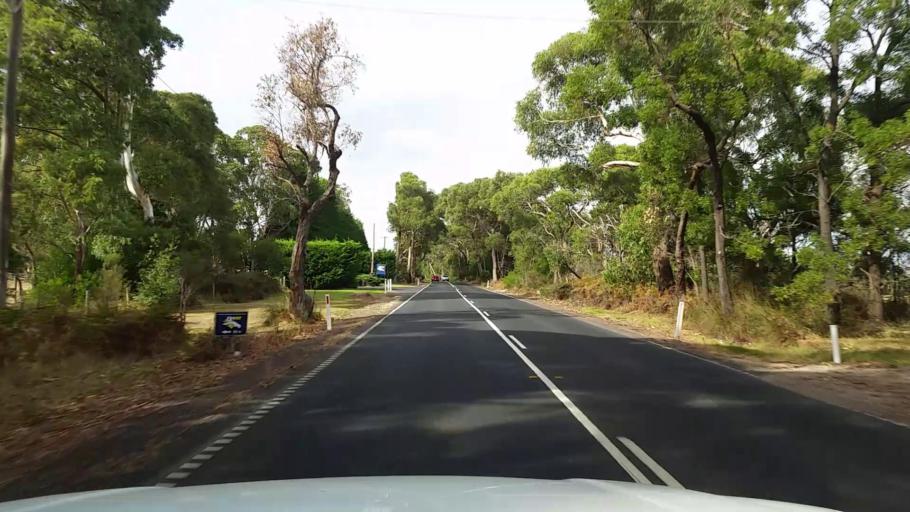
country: AU
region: Victoria
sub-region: Mornington Peninsula
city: Mount Martha
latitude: -38.3017
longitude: 145.0801
